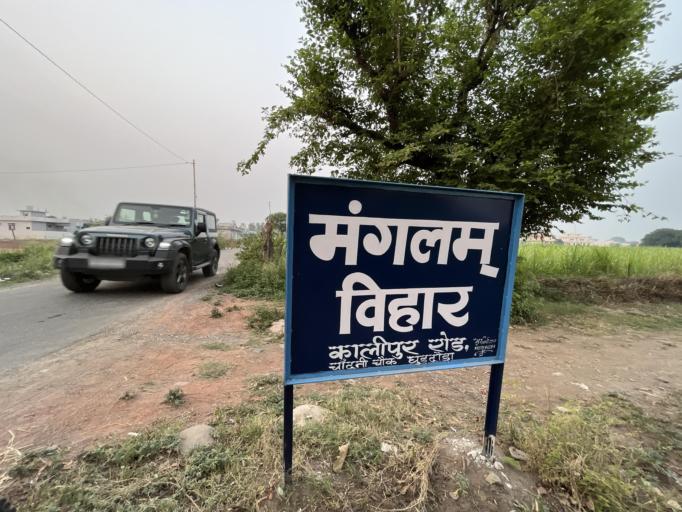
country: IN
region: Uttarakhand
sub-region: Naini Tal
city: Haldwani
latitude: 29.1662
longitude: 79.4796
